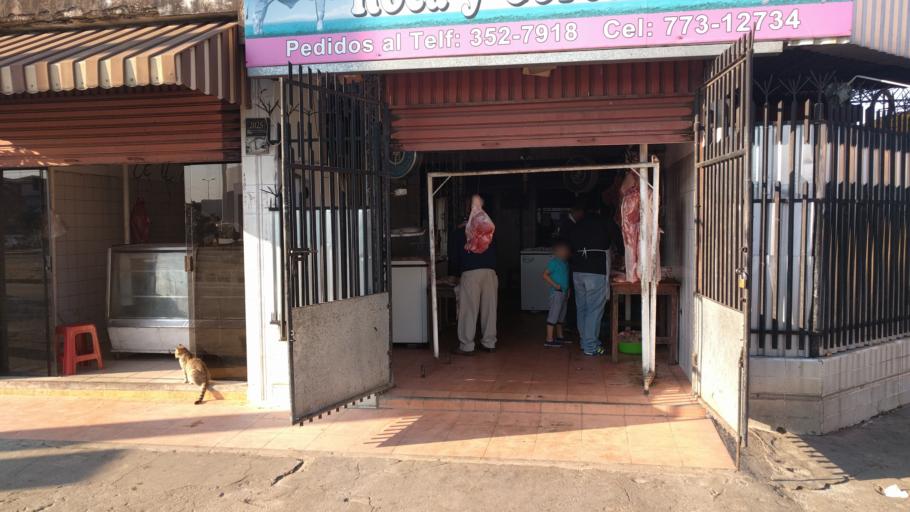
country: BO
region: Santa Cruz
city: Santa Cruz de la Sierra
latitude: -17.7854
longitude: -63.1959
